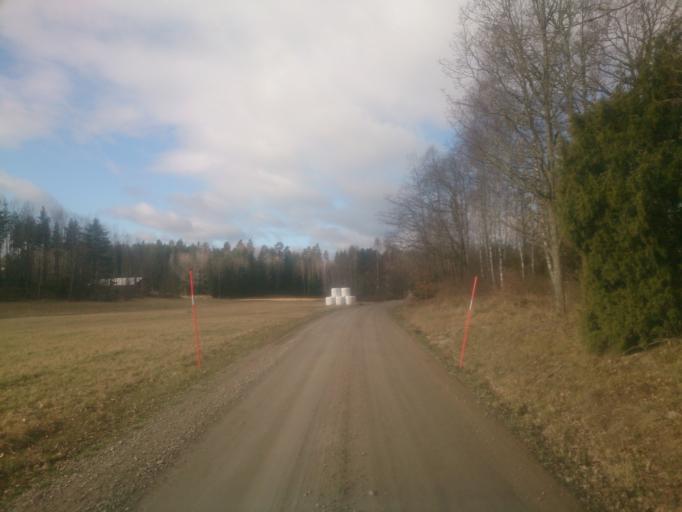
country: SE
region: OEstergoetland
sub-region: Atvidabergs Kommun
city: Atvidaberg
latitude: 58.2295
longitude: 16.1779
